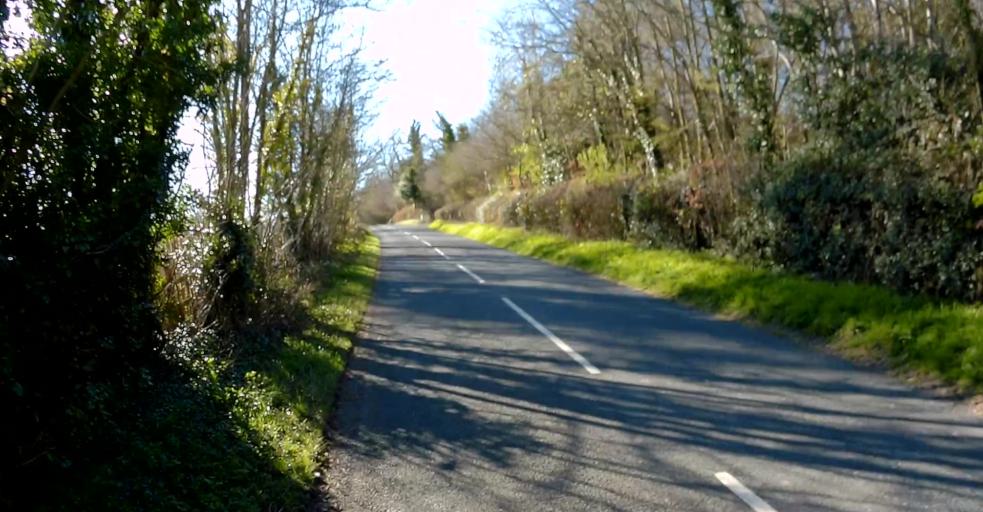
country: GB
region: England
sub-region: Hampshire
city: Basingstoke
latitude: 51.2496
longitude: -1.0596
